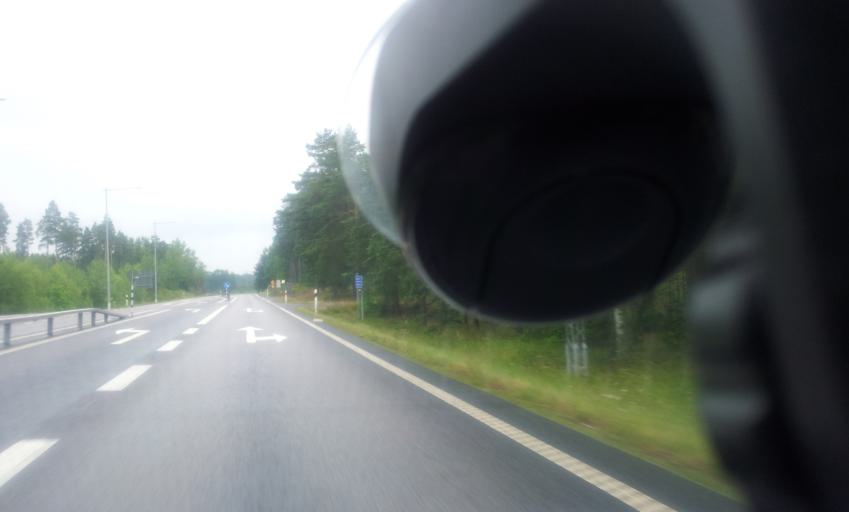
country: SE
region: Kalmar
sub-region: Vasterviks Kommun
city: Forserum
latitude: 57.9959
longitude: 16.4858
